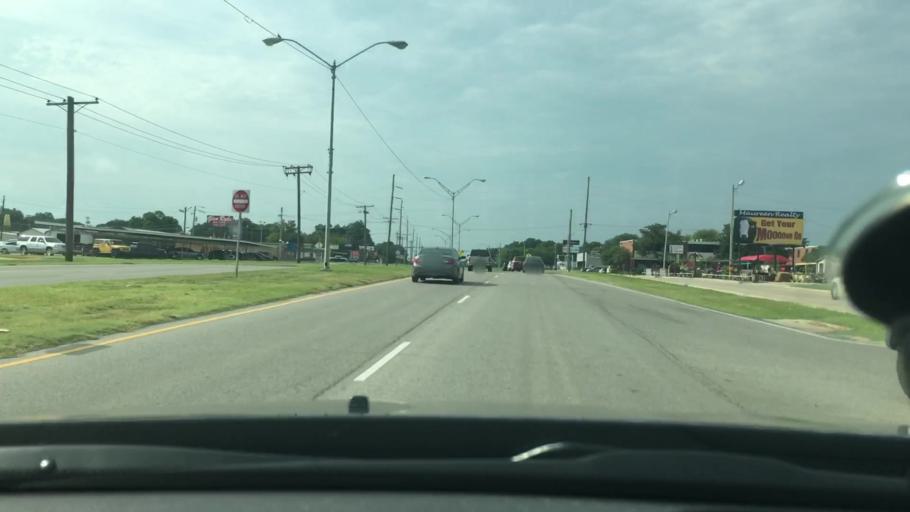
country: US
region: Oklahoma
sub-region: Carter County
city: Ardmore
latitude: 34.1777
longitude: -97.1433
